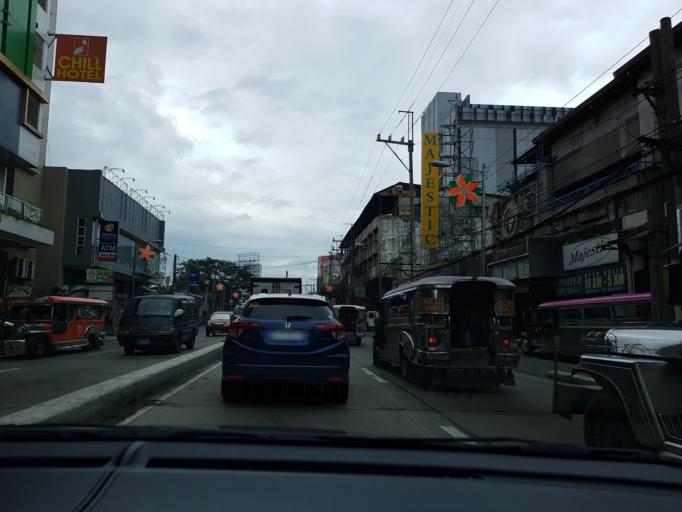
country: PH
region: Metro Manila
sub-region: Caloocan City
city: Niugan
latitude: 14.6597
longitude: 120.9840
